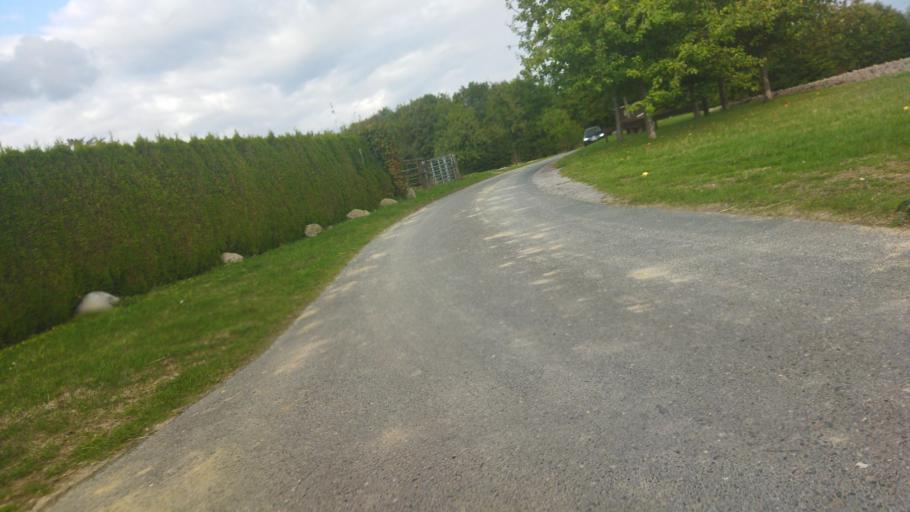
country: DE
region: North Rhine-Westphalia
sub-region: Regierungsbezirk Munster
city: Billerbeck
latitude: 51.9181
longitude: 7.2569
